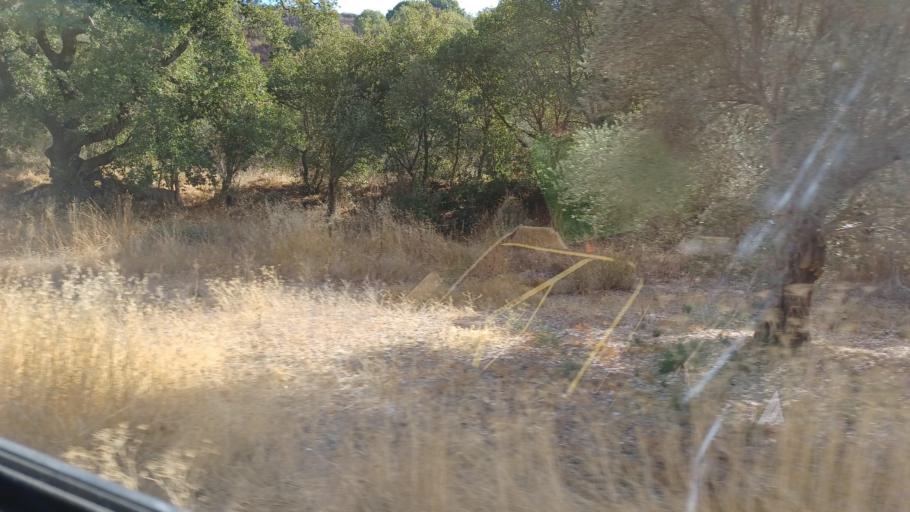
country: CY
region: Pafos
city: Tala
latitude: 34.9258
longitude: 32.4818
